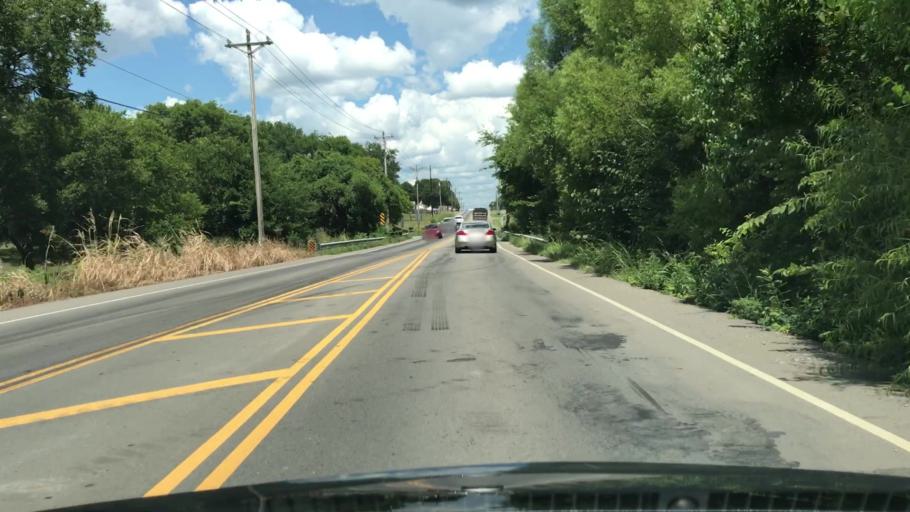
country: US
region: Tennessee
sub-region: Williamson County
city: Nolensville
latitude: 35.9431
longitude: -86.6640
